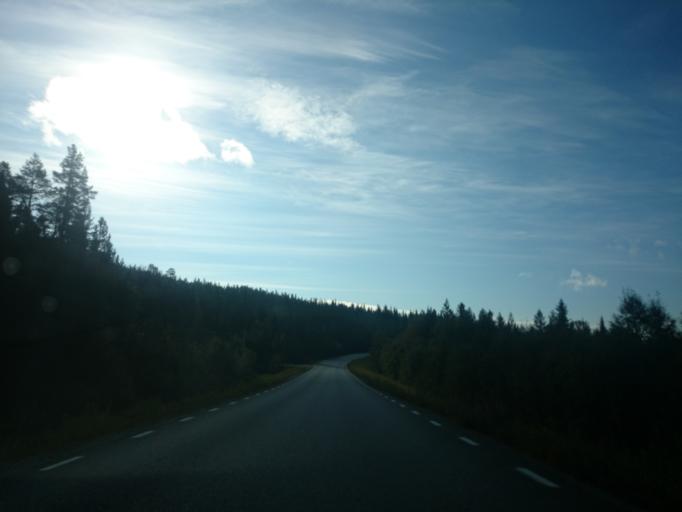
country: SE
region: Jaemtland
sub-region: Are Kommun
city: Are
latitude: 62.5841
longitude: 12.5560
